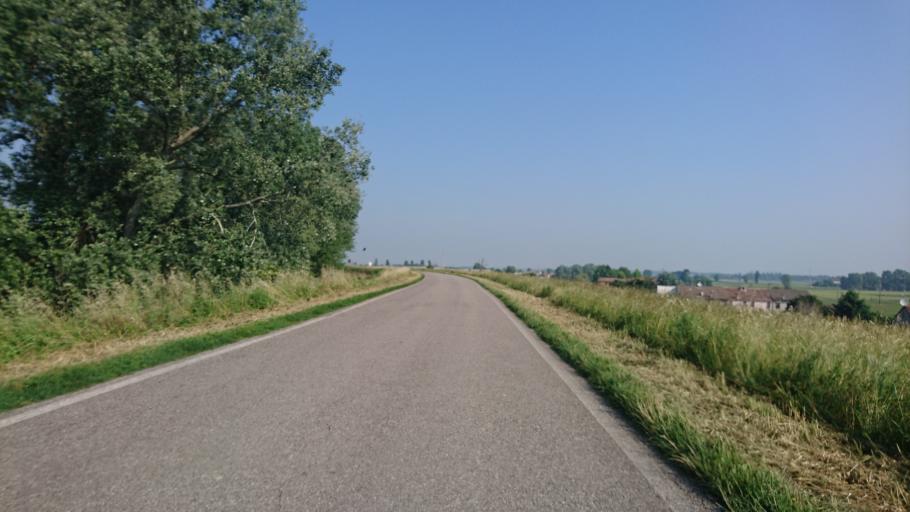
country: IT
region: Veneto
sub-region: Provincia di Rovigo
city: Bergantino
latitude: 45.0576
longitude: 11.2709
